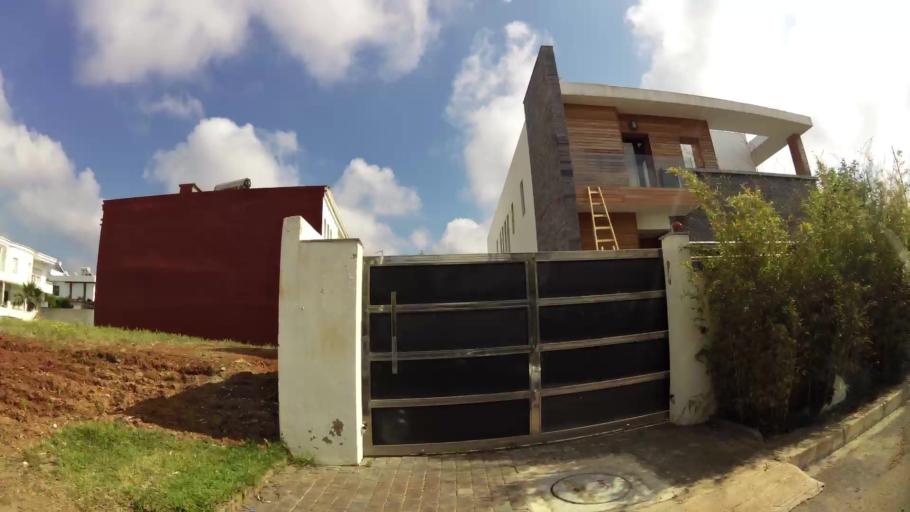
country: MA
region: Rabat-Sale-Zemmour-Zaer
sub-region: Skhirate-Temara
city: Temara
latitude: 33.9475
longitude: -6.8761
